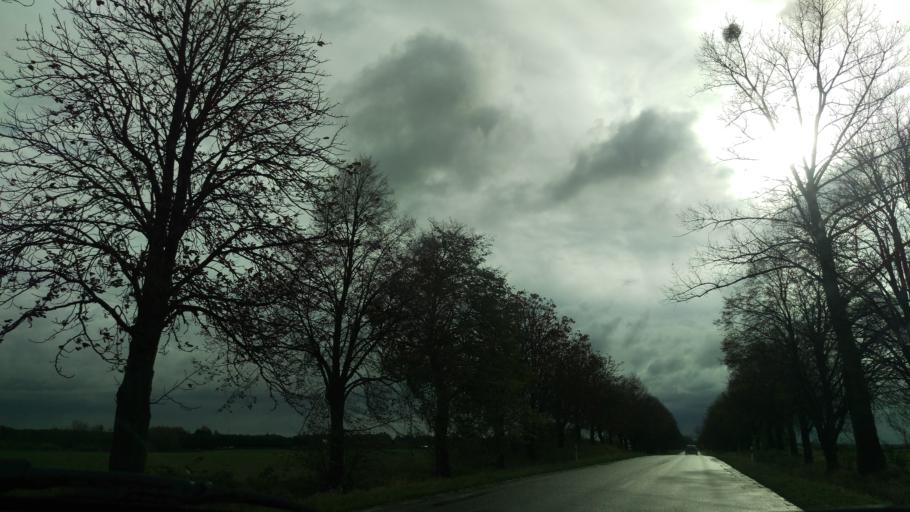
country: PL
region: West Pomeranian Voivodeship
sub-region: Powiat gryficki
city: Ploty
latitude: 53.8277
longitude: 15.2470
